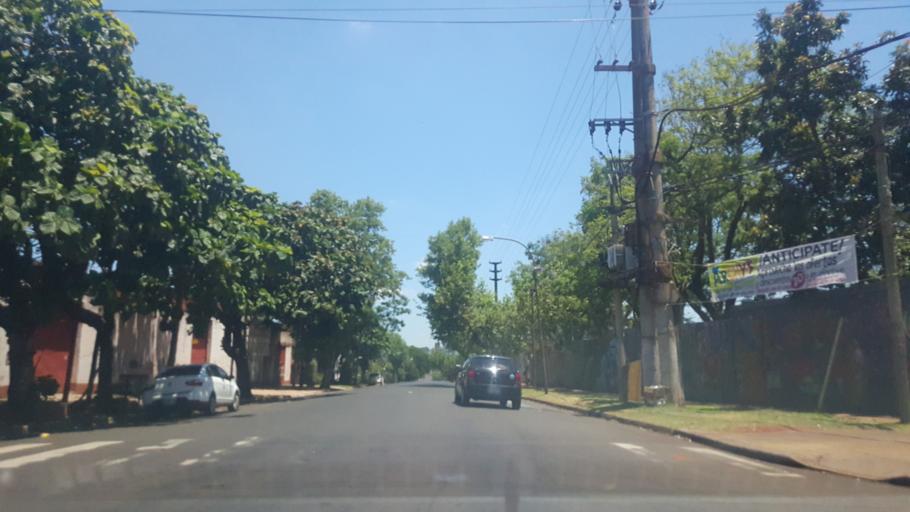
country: AR
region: Misiones
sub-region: Departamento de Capital
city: Posadas
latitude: -27.3739
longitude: -55.9023
